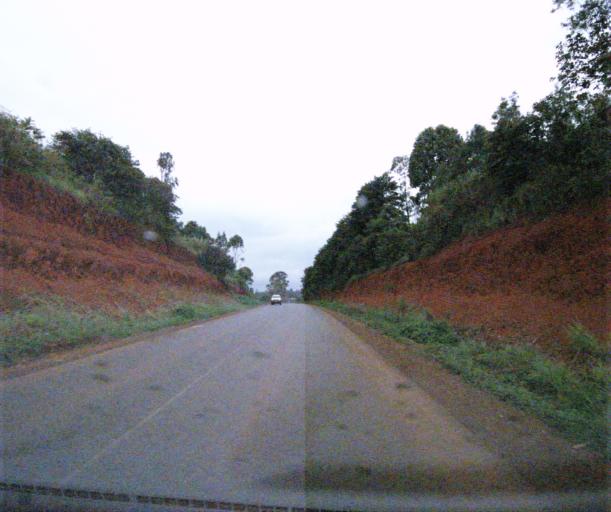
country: CM
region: West
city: Dschang
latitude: 5.4896
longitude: 10.1820
